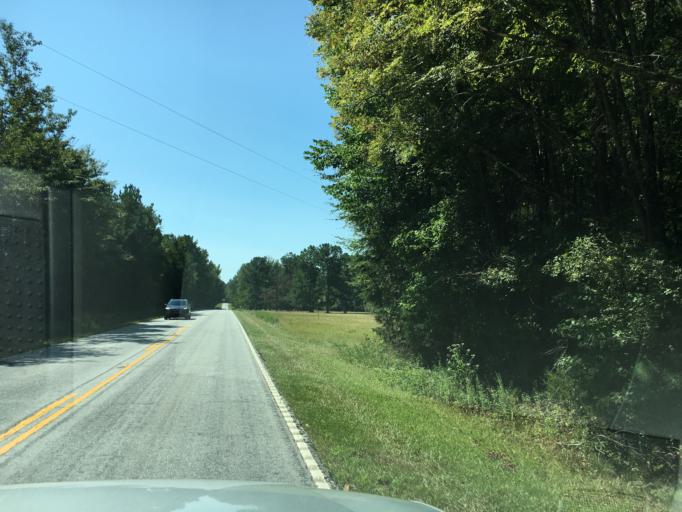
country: US
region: South Carolina
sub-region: Laurens County
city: Clinton
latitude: 34.4291
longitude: -81.8673
